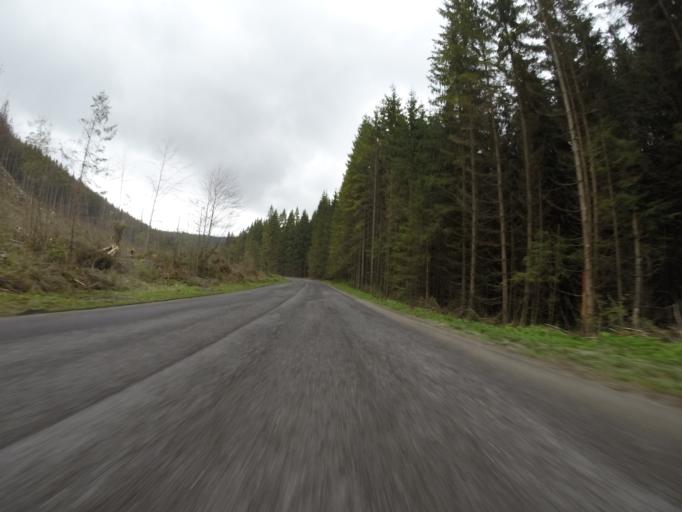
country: SK
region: Banskobystricky
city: Revuca
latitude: 48.8021
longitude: 20.1452
